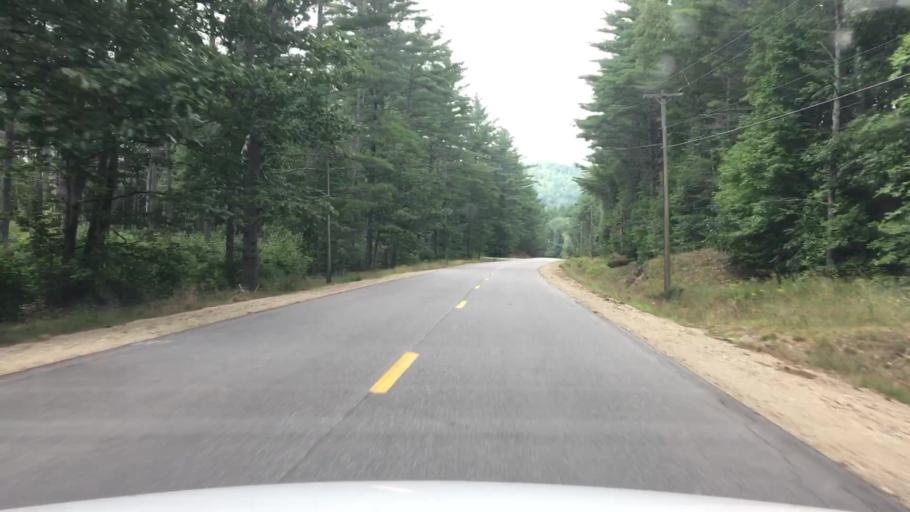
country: US
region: Maine
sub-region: Oxford County
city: Rumford
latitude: 44.5439
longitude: -70.6777
